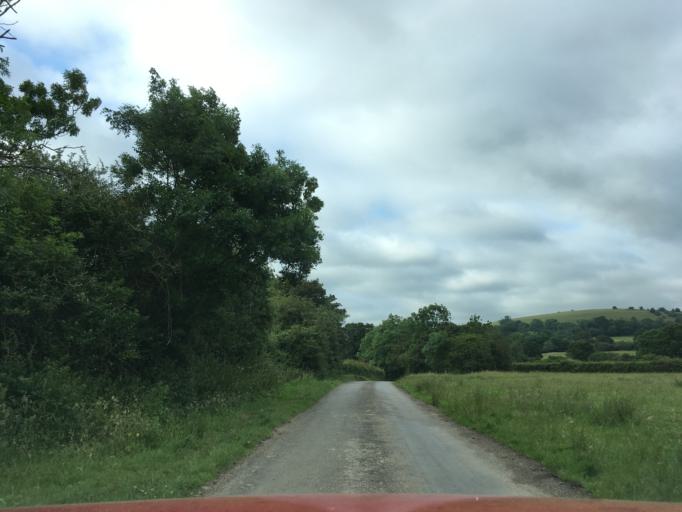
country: GB
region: England
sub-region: South Gloucestershire
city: Horton
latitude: 51.5827
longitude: -2.3463
